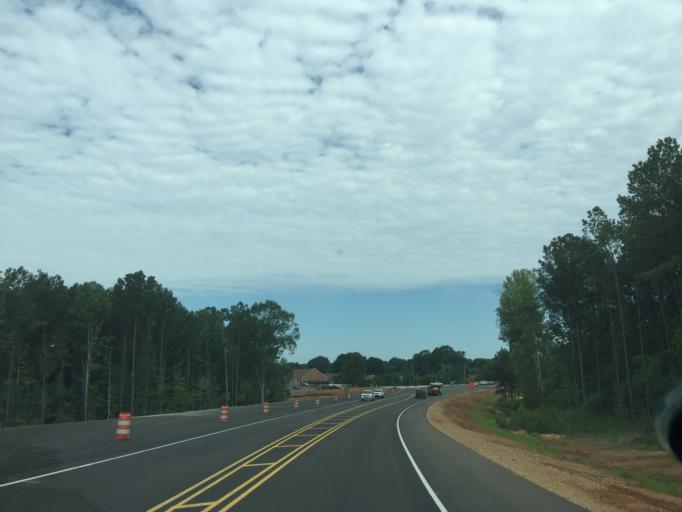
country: US
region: Mississippi
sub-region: Rankin County
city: Brandon
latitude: 32.2910
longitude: -89.9952
